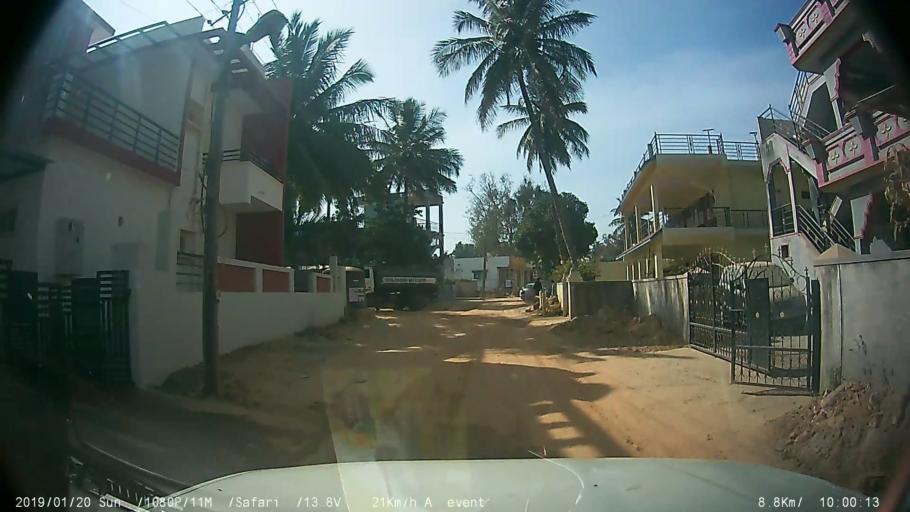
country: IN
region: Karnataka
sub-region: Bangalore Urban
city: Anekal
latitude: 12.8199
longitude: 77.6374
